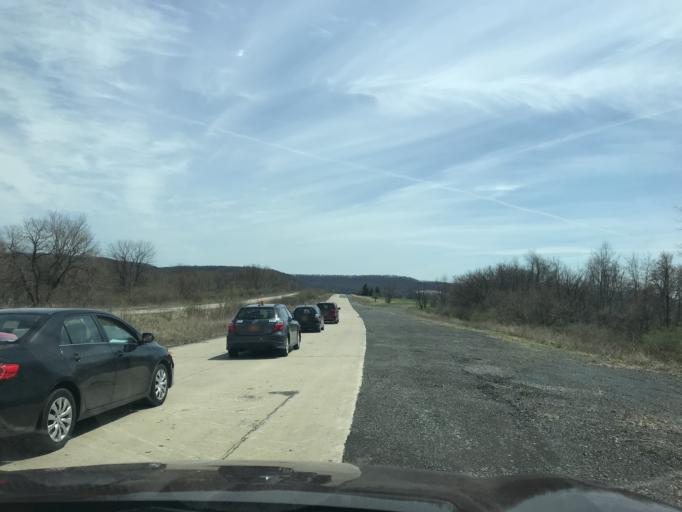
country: US
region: Pennsylvania
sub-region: Snyder County
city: Selinsgrove
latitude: 40.8219
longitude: -76.8571
